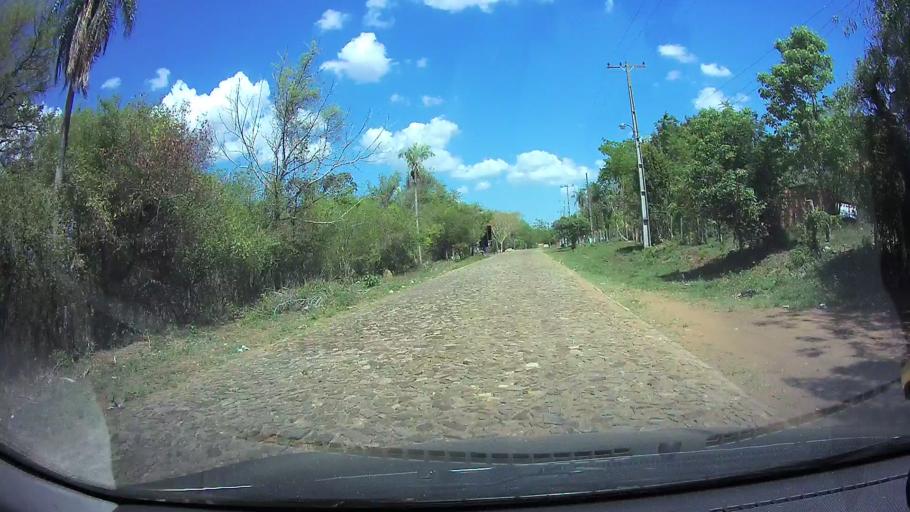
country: PY
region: Cordillera
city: Emboscada
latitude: -25.1168
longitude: -57.3063
